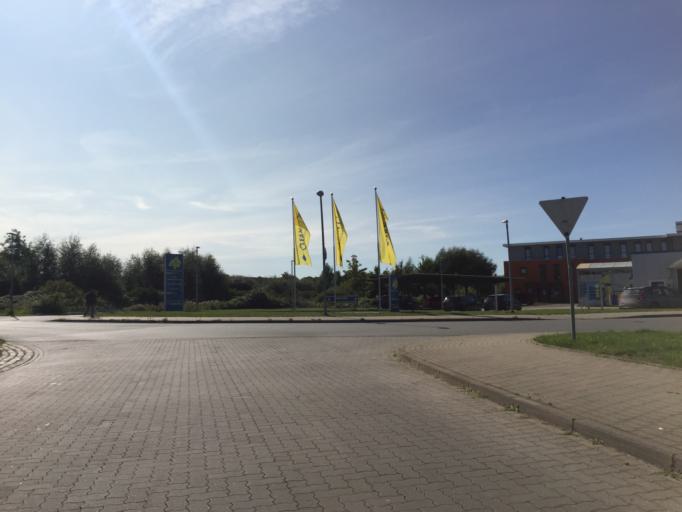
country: DE
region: Schleswig-Holstein
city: Itzehoe
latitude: 53.9144
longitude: 9.5135
